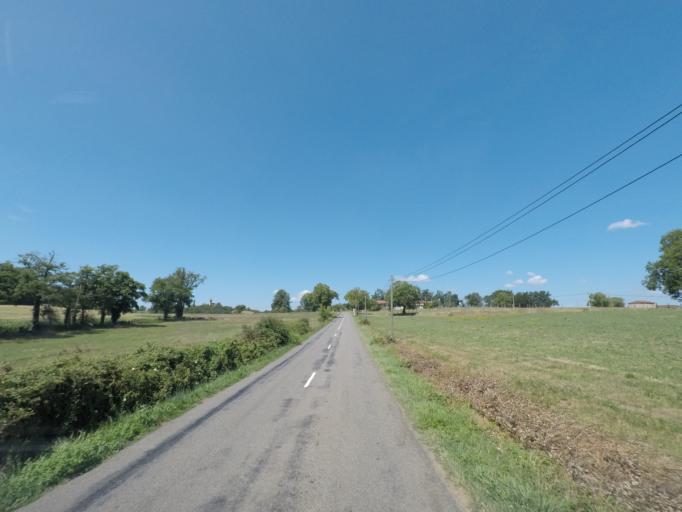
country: FR
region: Midi-Pyrenees
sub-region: Departement de l'Aveyron
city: Capdenac-Gare
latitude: 44.6198
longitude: 2.1169
